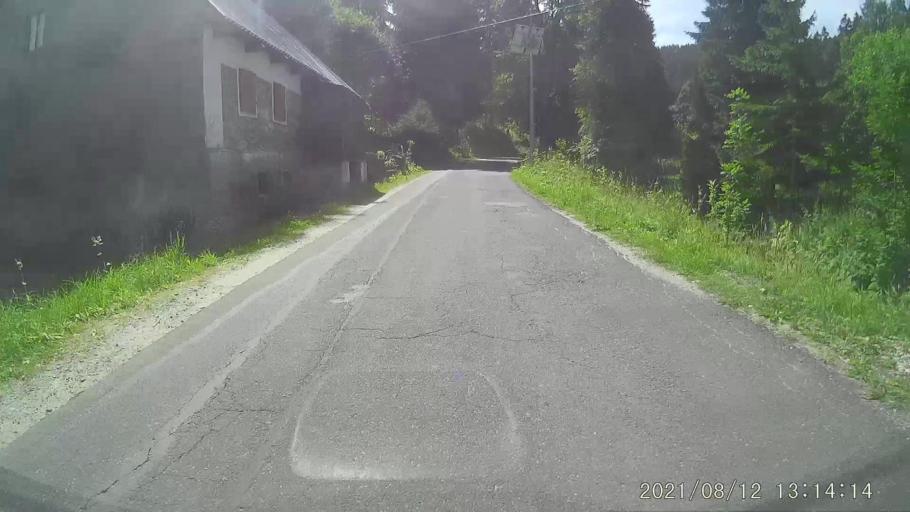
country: PL
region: Lower Silesian Voivodeship
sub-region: Powiat klodzki
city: Stronie Slaskie
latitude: 50.2578
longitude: 16.8584
